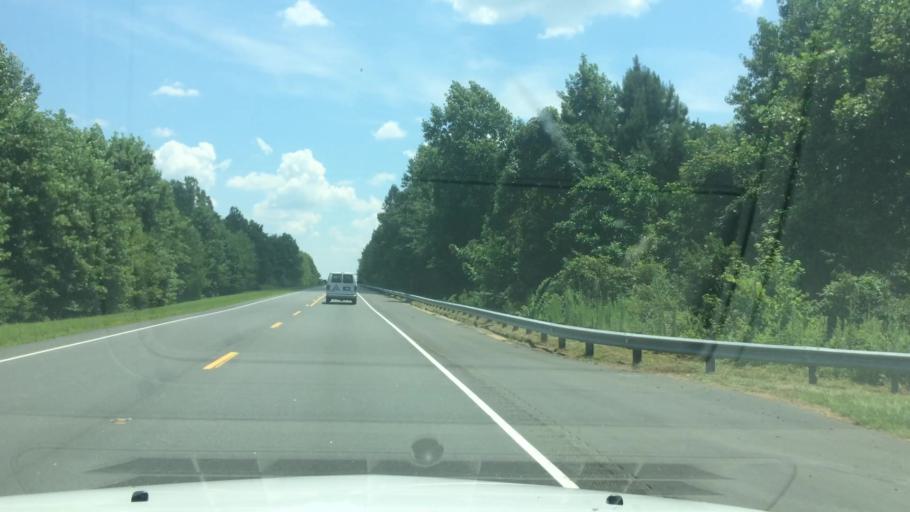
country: US
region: North Carolina
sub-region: Alexander County
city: Stony Point
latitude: 35.8410
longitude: -81.0254
